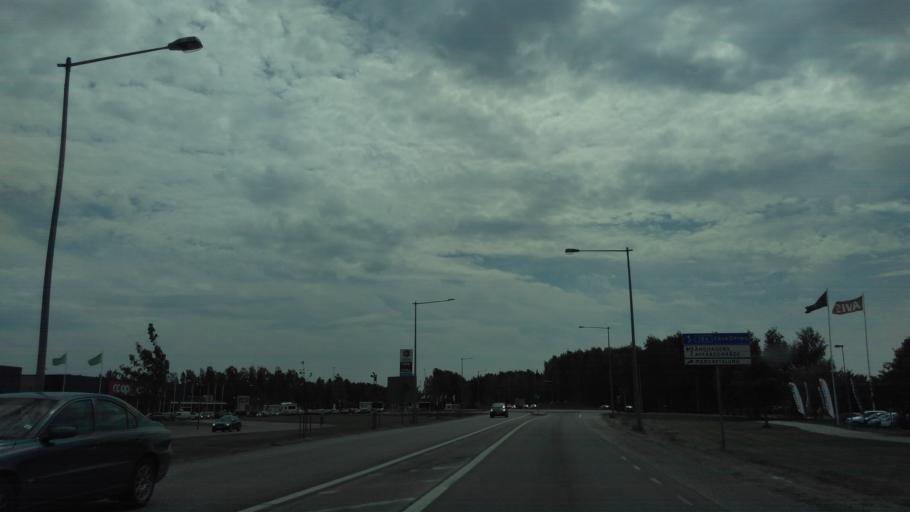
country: SE
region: Vaestra Goetaland
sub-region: Lidkopings Kommun
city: Lidkoping
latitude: 58.4954
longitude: 13.1815
